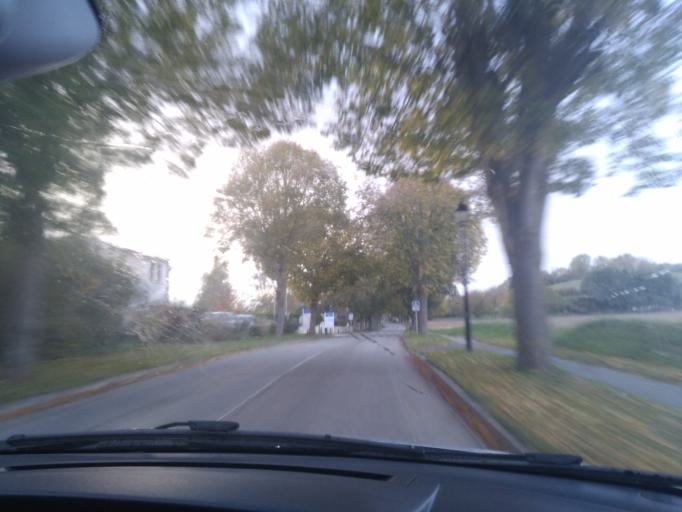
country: FR
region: Ile-de-France
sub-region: Departement des Yvelines
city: Chavenay
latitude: 48.8546
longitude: 1.9818
